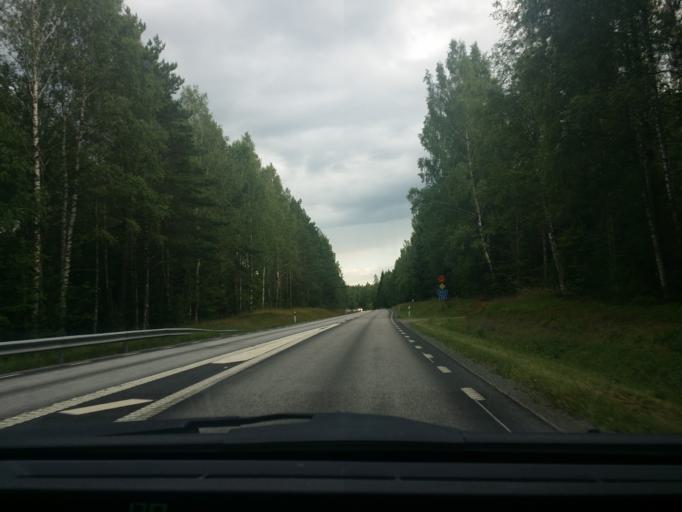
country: SE
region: OErebro
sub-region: Nora Kommun
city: Nora
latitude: 59.4896
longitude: 15.0610
